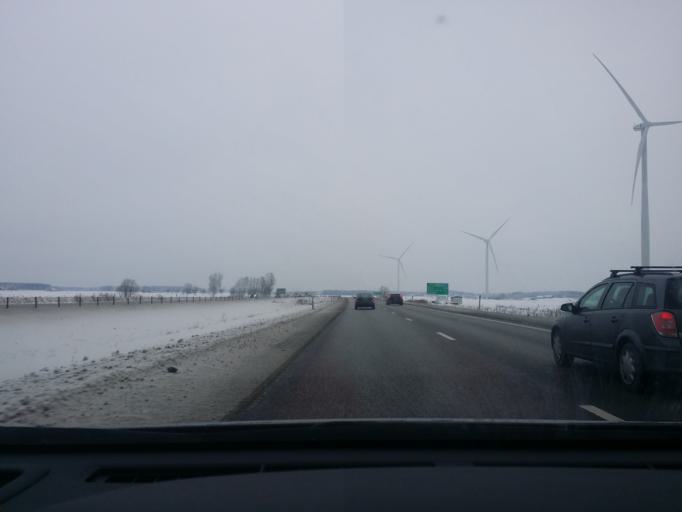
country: SE
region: OErebro
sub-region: Kumla Kommun
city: Kumla
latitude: 59.1741
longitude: 15.1173
